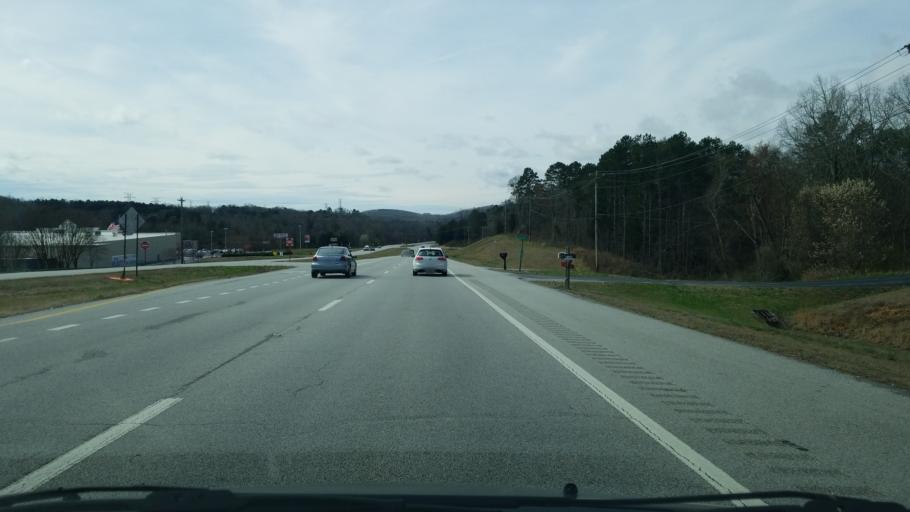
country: US
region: Tennessee
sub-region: Hamilton County
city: Lakesite
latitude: 35.1716
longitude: -85.0753
